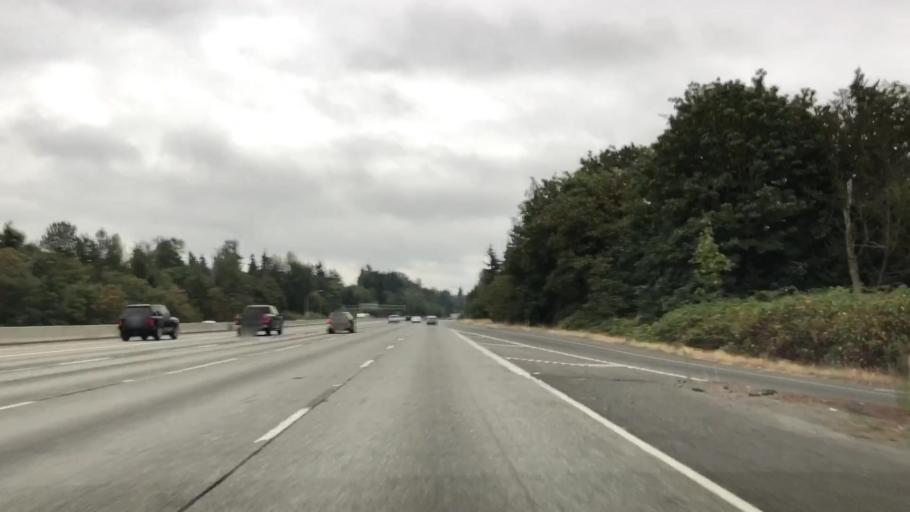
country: US
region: Washington
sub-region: King County
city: Des Moines
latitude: 47.3903
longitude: -122.2910
